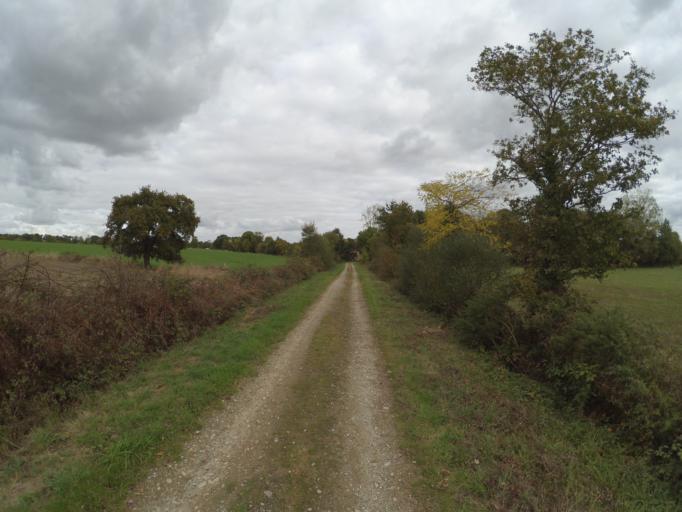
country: FR
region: Pays de la Loire
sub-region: Departement de la Loire-Atlantique
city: Remouille
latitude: 47.0489
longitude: -1.3512
